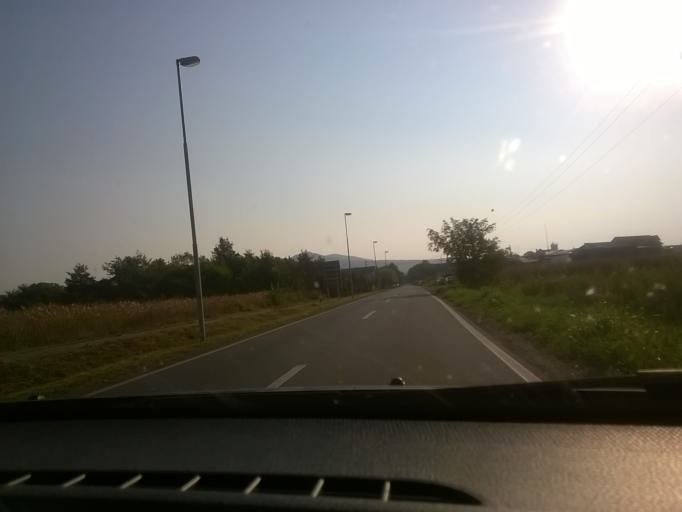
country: RS
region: Autonomna Pokrajina Vojvodina
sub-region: Juznobanatski Okrug
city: Vrsac
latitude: 45.1126
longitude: 21.2721
